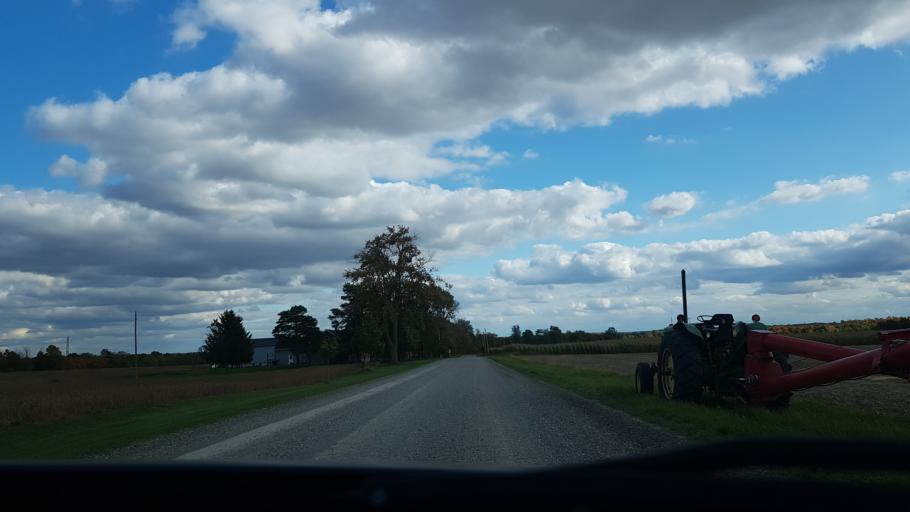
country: CA
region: Ontario
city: South Huron
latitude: 43.1010
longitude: -81.6012
